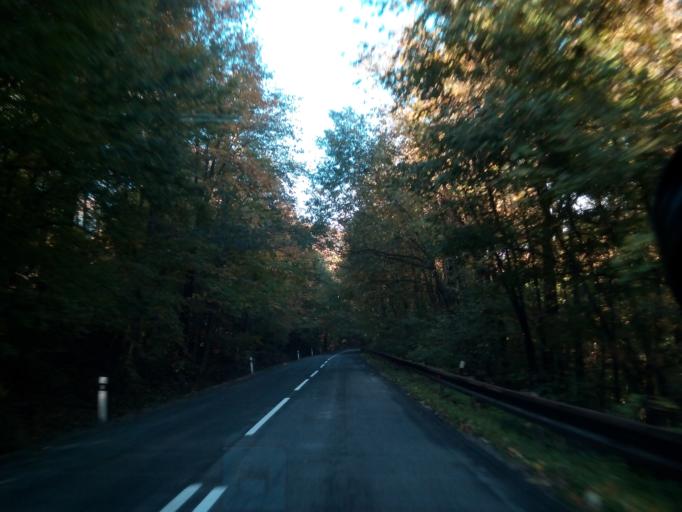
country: SK
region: Kosicky
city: Gelnica
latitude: 48.8328
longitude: 21.0575
